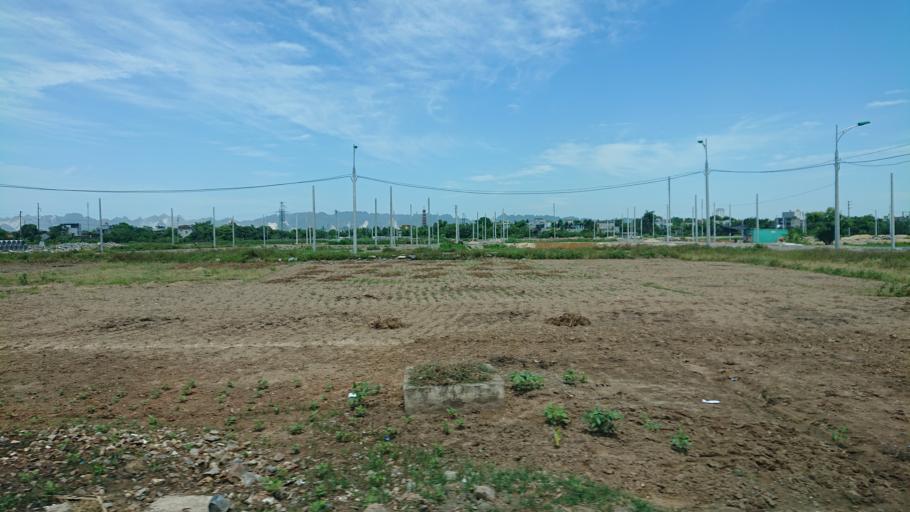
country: VN
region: Ha Nam
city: Thanh Pho Phu Ly
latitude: 20.5340
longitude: 105.9455
